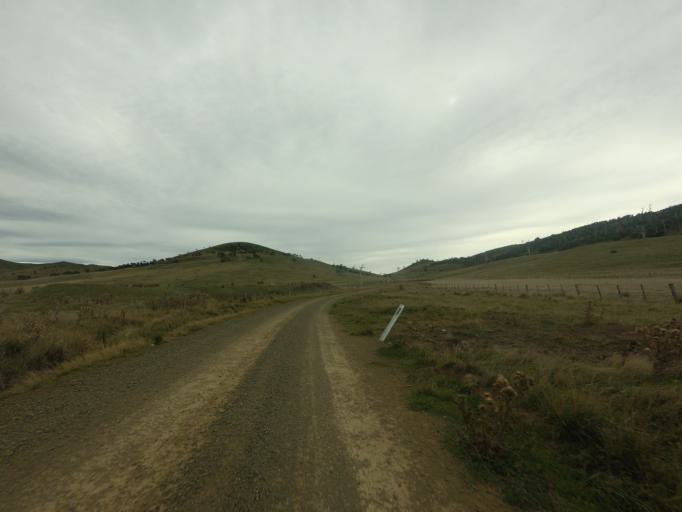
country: AU
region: Tasmania
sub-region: Derwent Valley
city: New Norfolk
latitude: -42.3817
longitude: 146.8686
